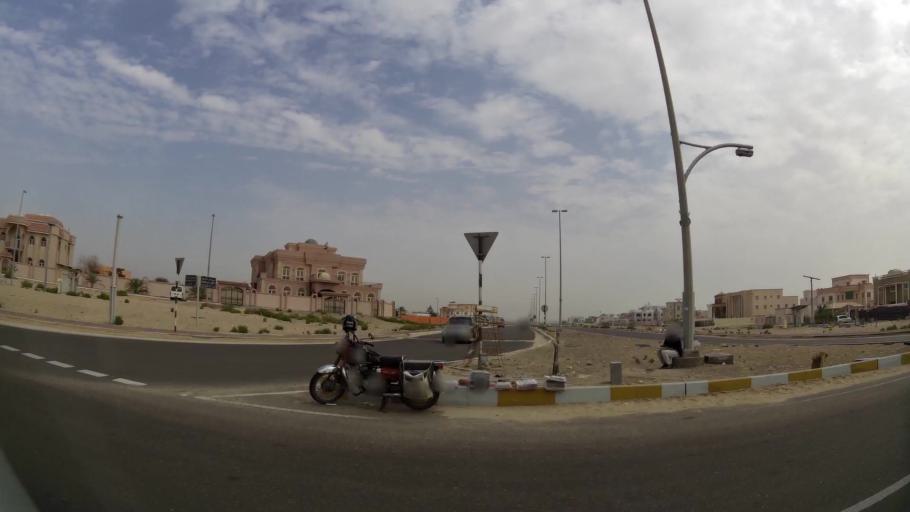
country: AE
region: Abu Dhabi
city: Abu Dhabi
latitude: 24.3105
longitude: 54.6429
